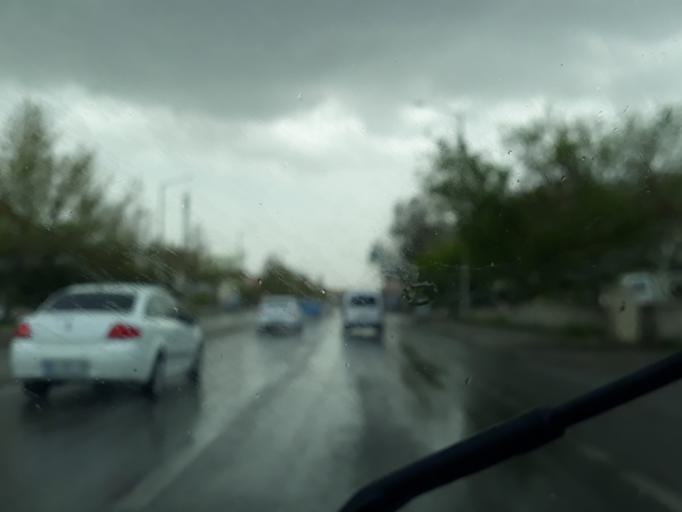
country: TR
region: Konya
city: Selcuklu
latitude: 37.9209
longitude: 32.4925
